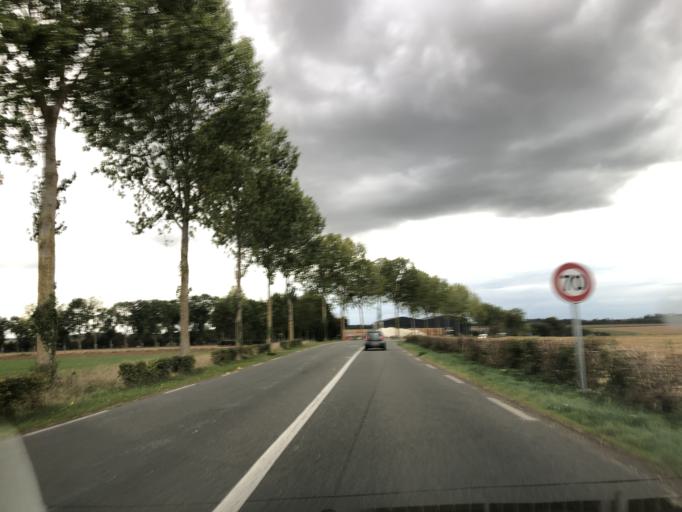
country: FR
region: Picardie
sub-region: Departement de la Somme
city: Chepy
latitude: 50.0987
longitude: 1.7323
